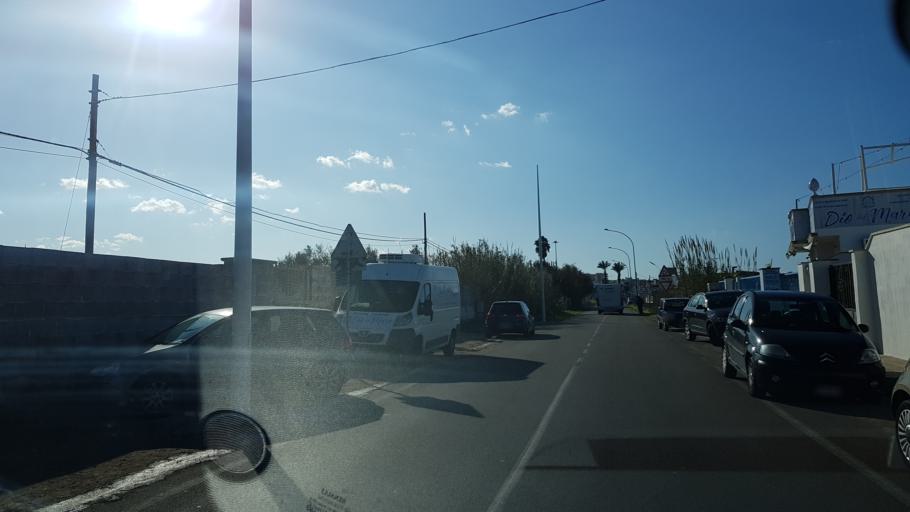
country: IT
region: Apulia
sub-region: Provincia di Lecce
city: Gallipoli
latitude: 40.0702
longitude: 18.0046
